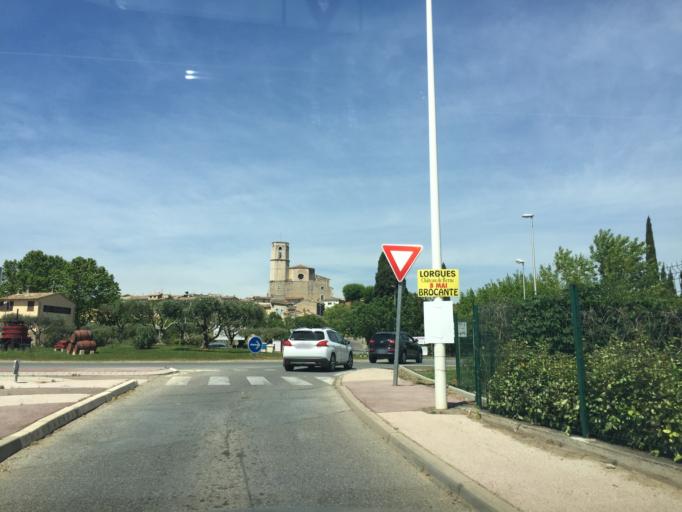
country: FR
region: Provence-Alpes-Cote d'Azur
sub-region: Departement du Var
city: Lorgues
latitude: 43.4897
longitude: 6.3644
